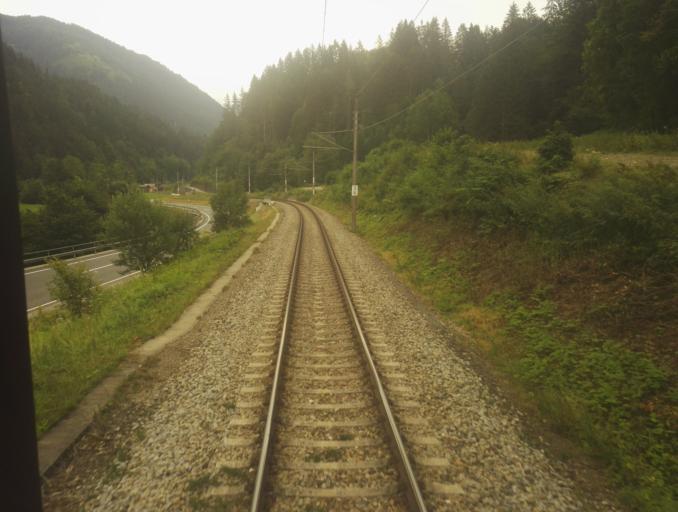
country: AT
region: Salzburg
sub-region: Politischer Bezirk Sankt Johann im Pongau
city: Bischofshofen
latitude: 47.4307
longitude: 13.2459
